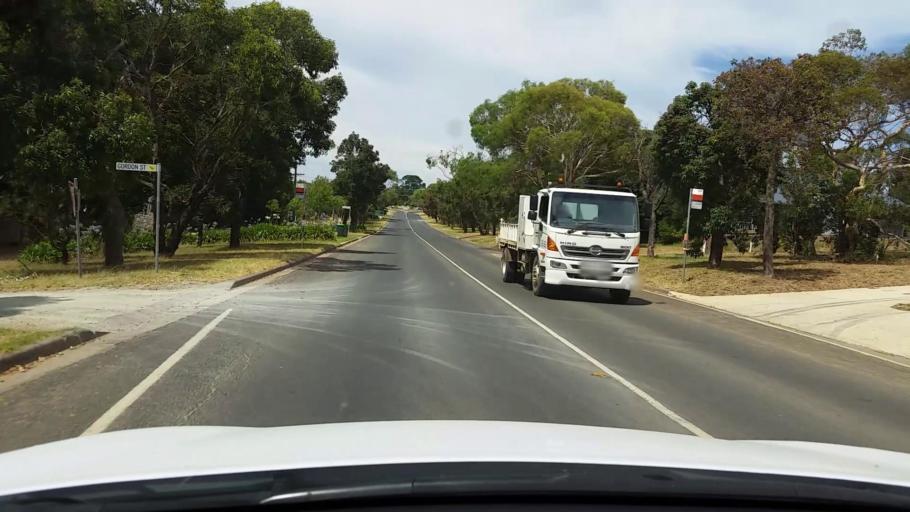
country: AU
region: Victoria
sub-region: Mornington Peninsula
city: Merricks
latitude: -38.4708
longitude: 145.0196
